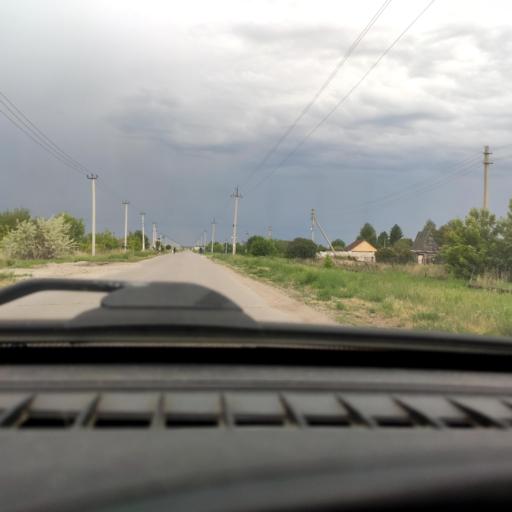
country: RU
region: Samara
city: Tol'yatti
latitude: 53.6433
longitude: 49.3291
